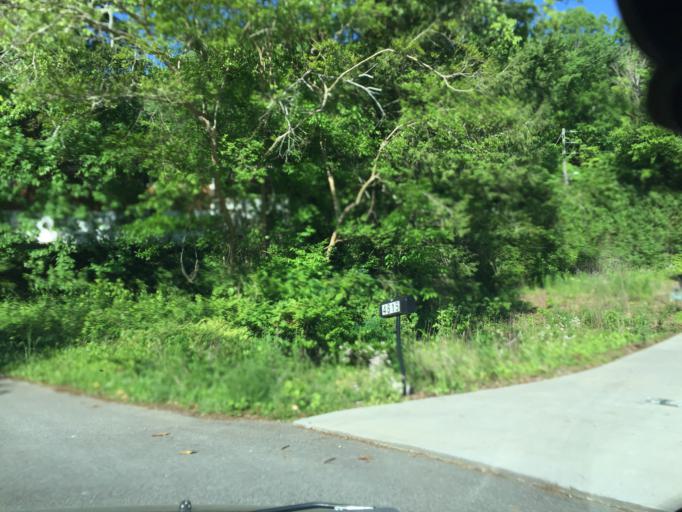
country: US
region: Tennessee
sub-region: Hamilton County
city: Lookout Mountain
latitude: 34.9947
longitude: -85.3317
